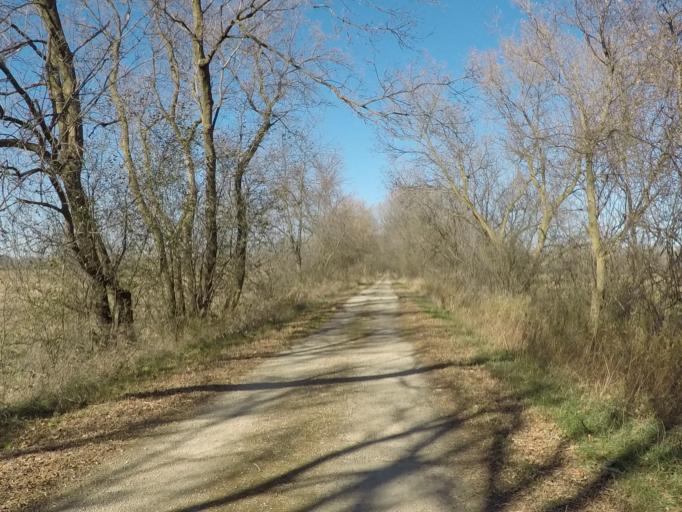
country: US
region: Wisconsin
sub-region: Dane County
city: Deerfield
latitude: 43.0461
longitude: -89.0546
